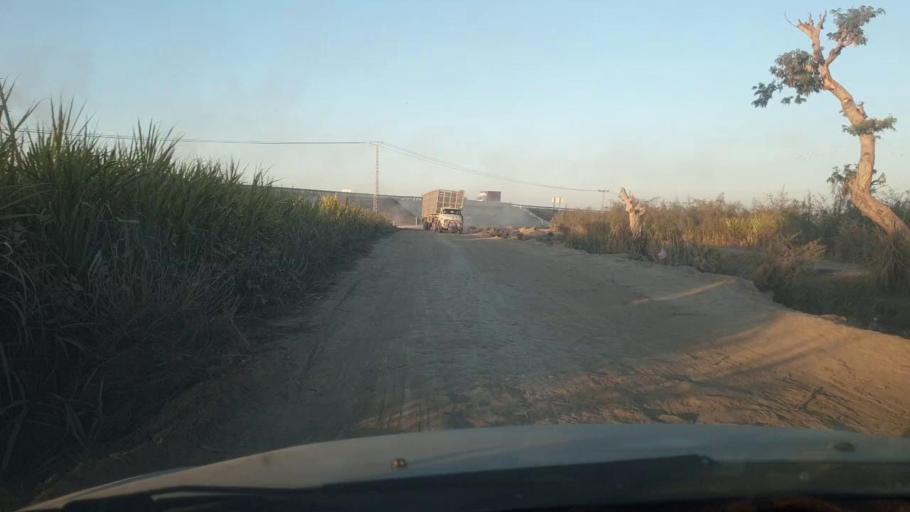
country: PK
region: Sindh
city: Ghotki
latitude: 28.0429
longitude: 69.3249
